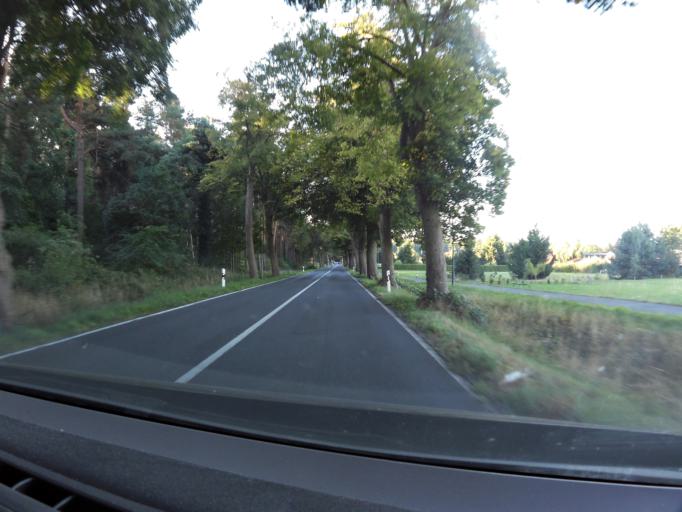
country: DE
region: Mecklenburg-Vorpommern
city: Usedom
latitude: 53.9137
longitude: 14.0191
